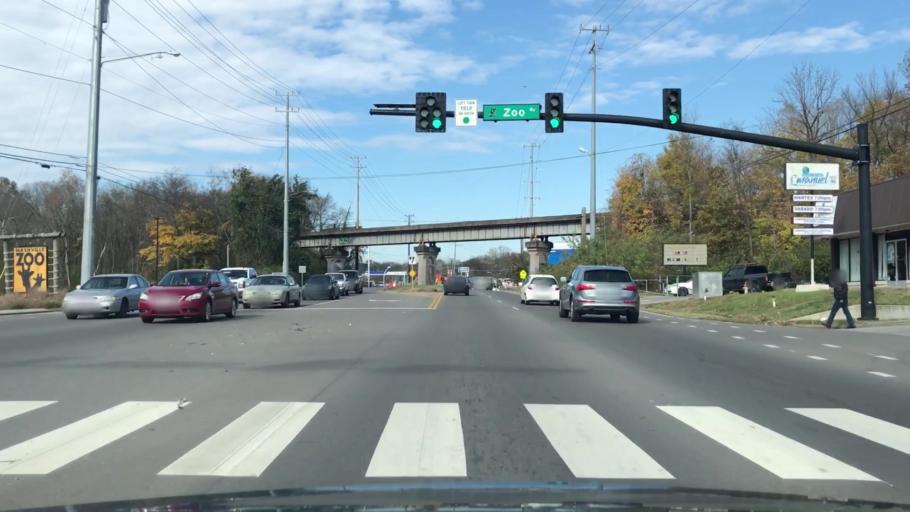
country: US
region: Tennessee
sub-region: Davidson County
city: Oak Hill
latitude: 36.0900
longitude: -86.7335
